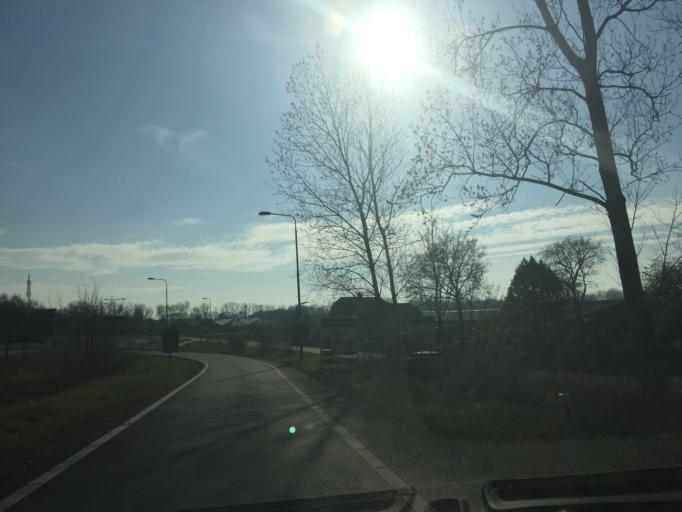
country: NL
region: South Holland
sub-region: Gemeente Noordwijkerhout
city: Noordwijkerhout
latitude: 52.2709
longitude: 4.5034
